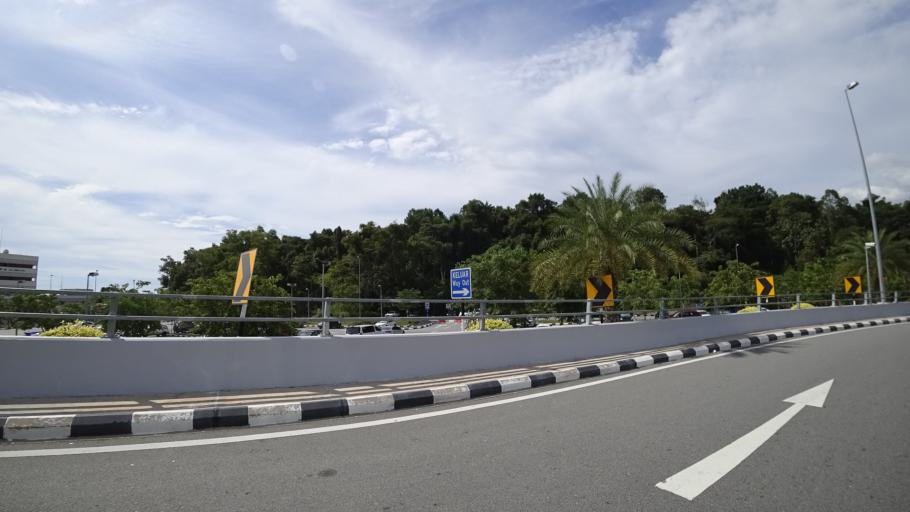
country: BN
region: Brunei and Muara
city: Bandar Seri Begawan
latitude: 4.9453
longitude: 114.9354
